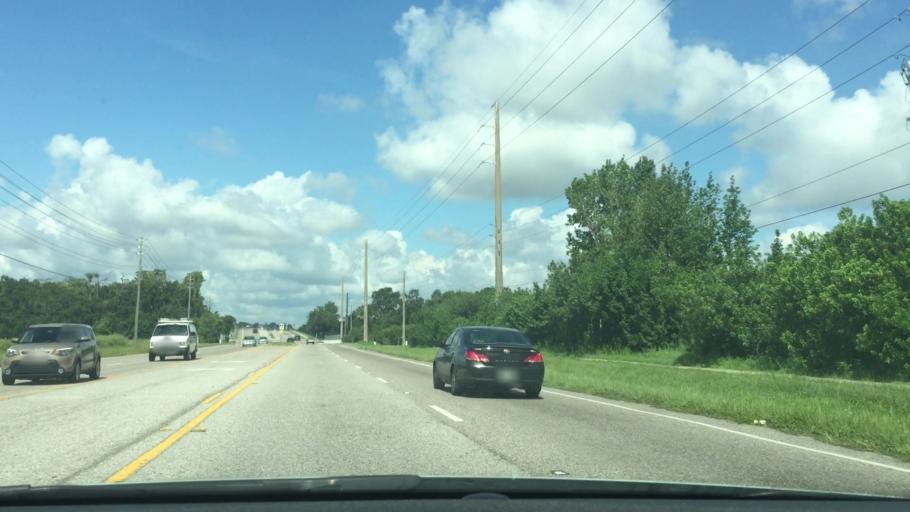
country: US
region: Florida
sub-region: Osceola County
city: Buenaventura Lakes
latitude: 28.3056
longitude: -81.3575
